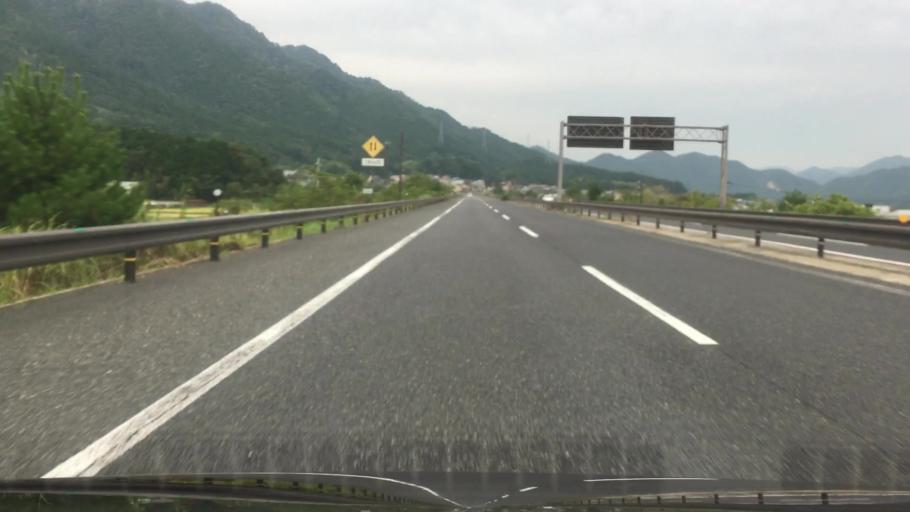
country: JP
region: Kyoto
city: Fukuchiyama
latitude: 35.1636
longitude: 135.1073
